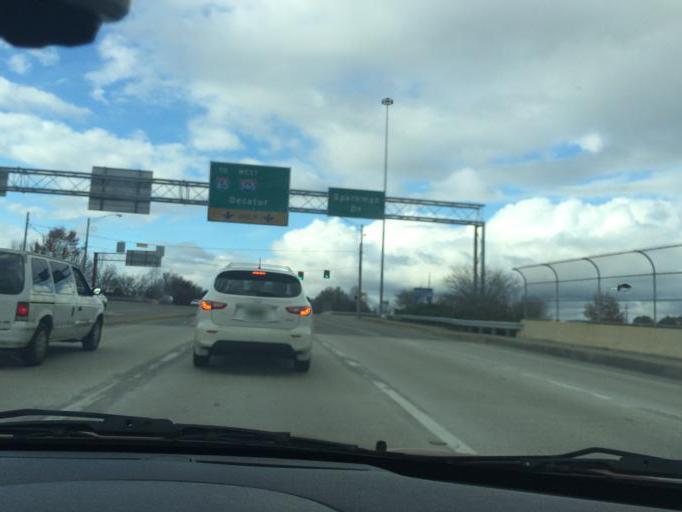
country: US
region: Alabama
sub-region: Madison County
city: Redstone Arsenal
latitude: 34.7149
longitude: -86.6435
